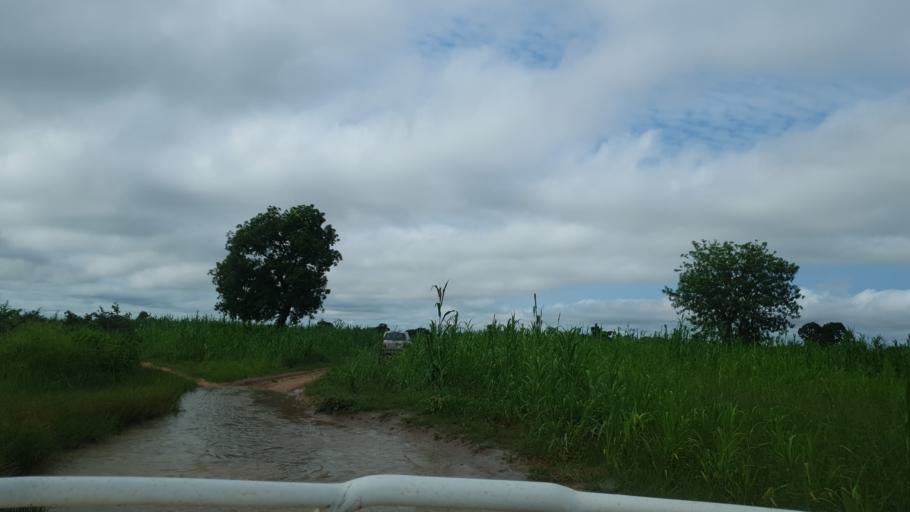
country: ML
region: Segou
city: Baroueli
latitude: 13.4965
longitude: -6.8968
